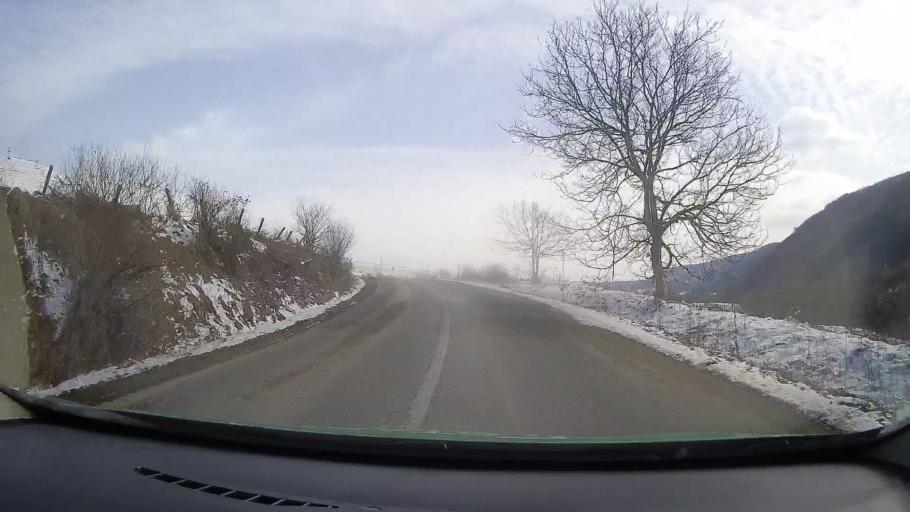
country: RO
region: Mures
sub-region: Comuna Apold
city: Saes
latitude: 46.1631
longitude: 24.7596
